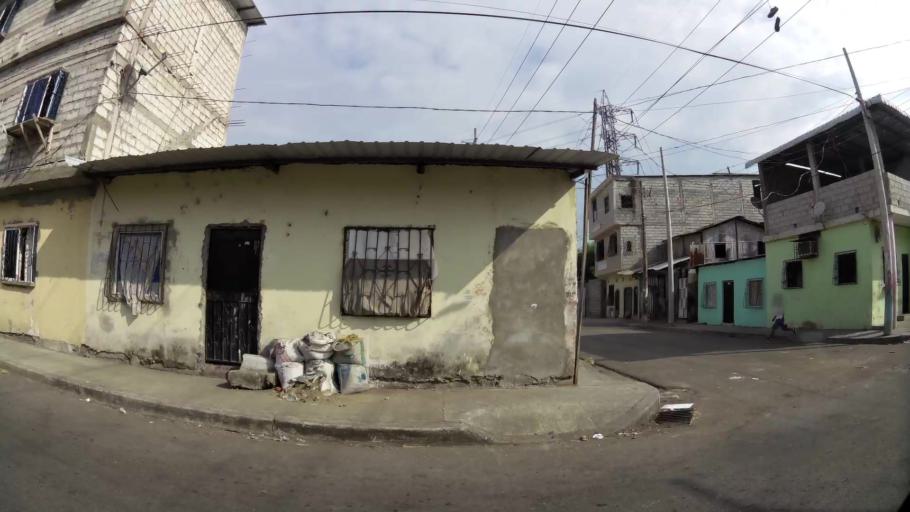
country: EC
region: Guayas
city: Guayaquil
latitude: -2.2493
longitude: -79.9098
